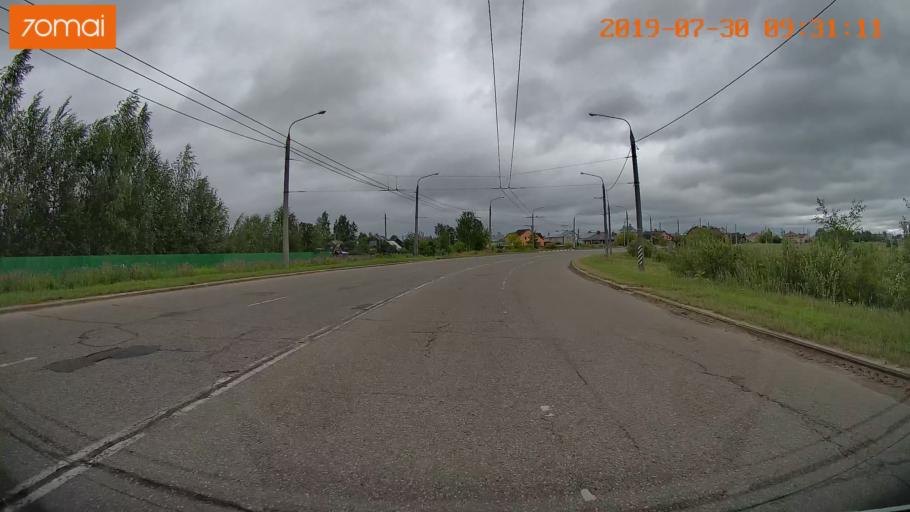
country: RU
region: Ivanovo
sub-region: Gorod Ivanovo
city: Ivanovo
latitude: 56.9527
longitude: 40.9501
